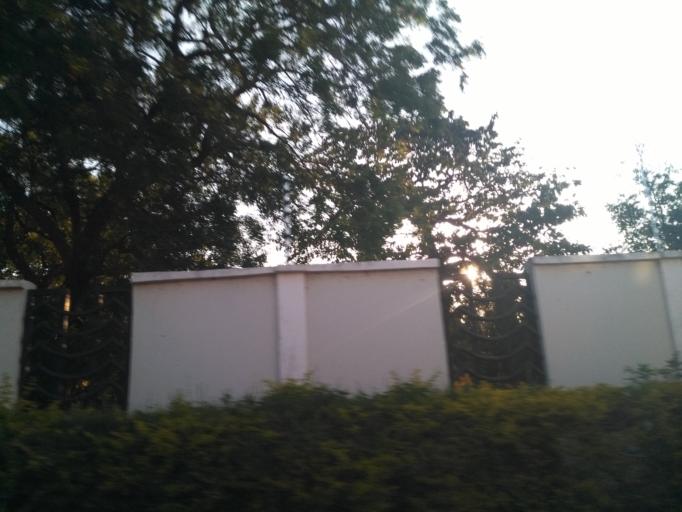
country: TZ
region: Dar es Salaam
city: Magomeni
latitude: -6.7764
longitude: 39.2803
